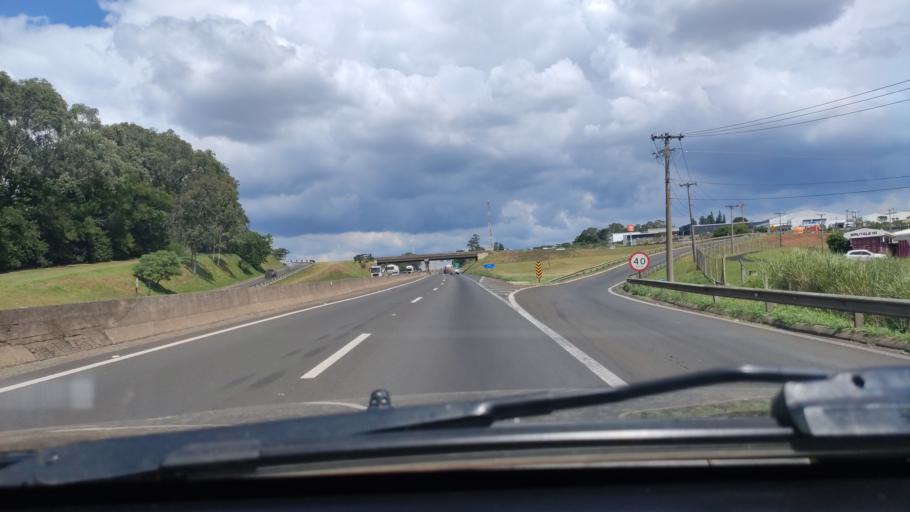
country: BR
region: Sao Paulo
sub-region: Sao Carlos
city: Sao Carlos
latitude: -22.0339
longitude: -47.8606
